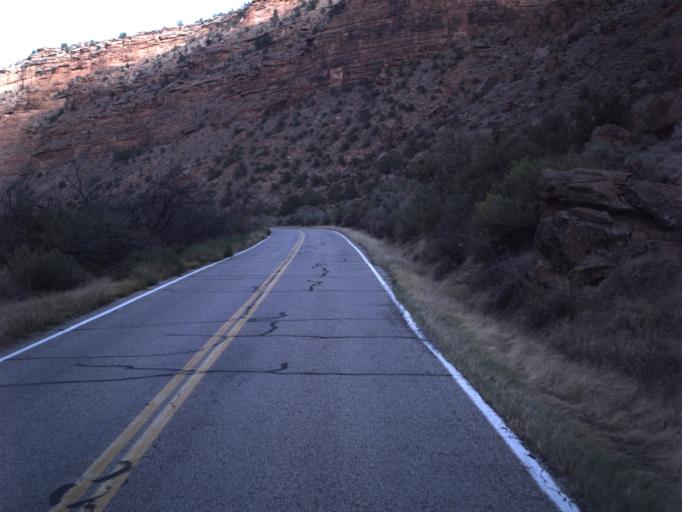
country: US
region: Utah
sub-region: Grand County
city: Moab
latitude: 38.7947
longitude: -109.3268
